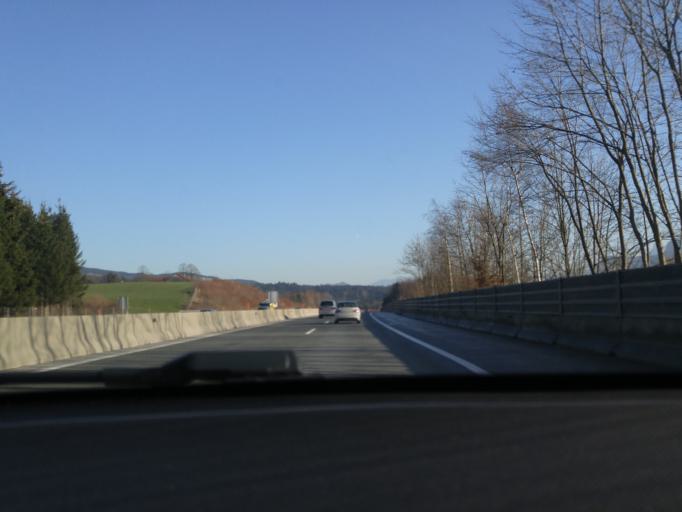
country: AT
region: Salzburg
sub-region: Politischer Bezirk Salzburg-Umgebung
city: Plainfeld
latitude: 47.8560
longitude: 13.2031
